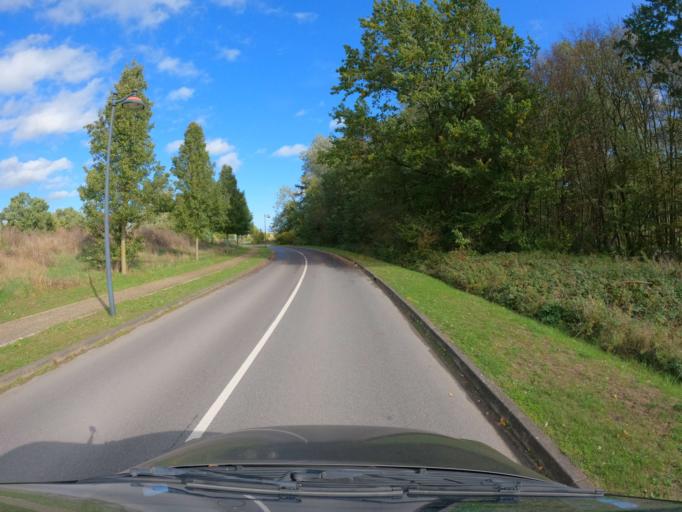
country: FR
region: Ile-de-France
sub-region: Departement de Seine-et-Marne
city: Coupvray
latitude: 48.8876
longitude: 2.8110
